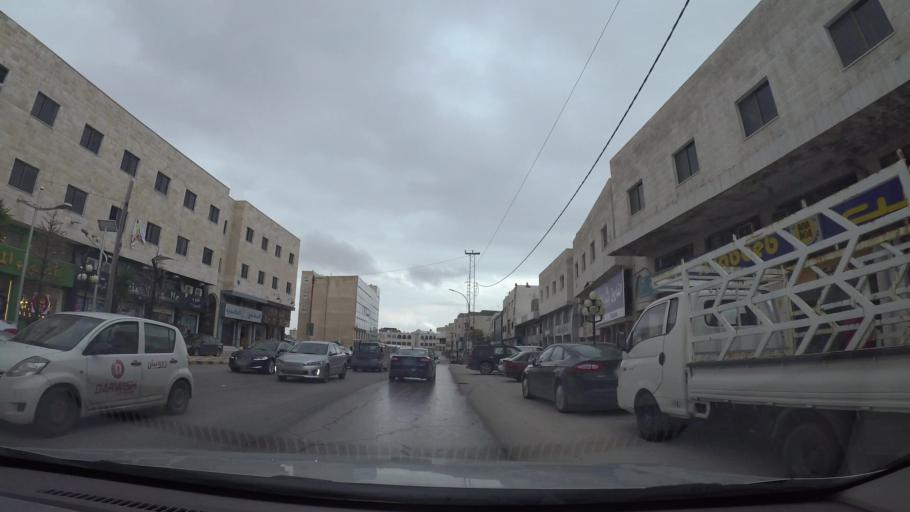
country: JO
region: Amman
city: Wadi as Sir
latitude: 31.9791
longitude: 35.8491
